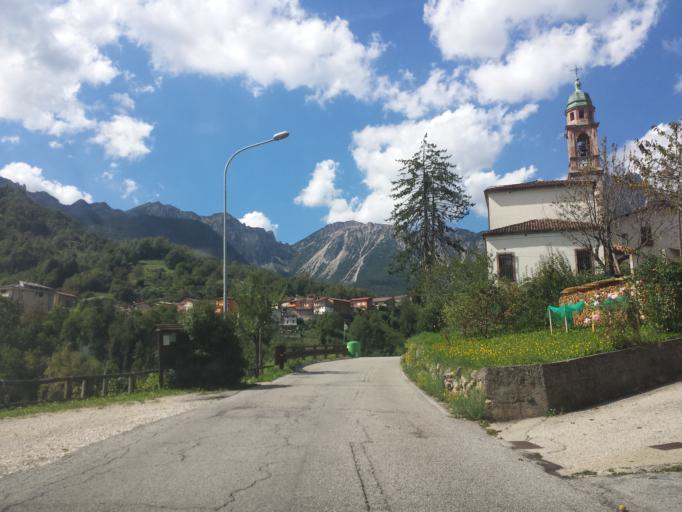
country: IT
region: Veneto
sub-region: Provincia di Vicenza
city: Recoaro Terme
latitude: 45.7018
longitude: 11.2054
